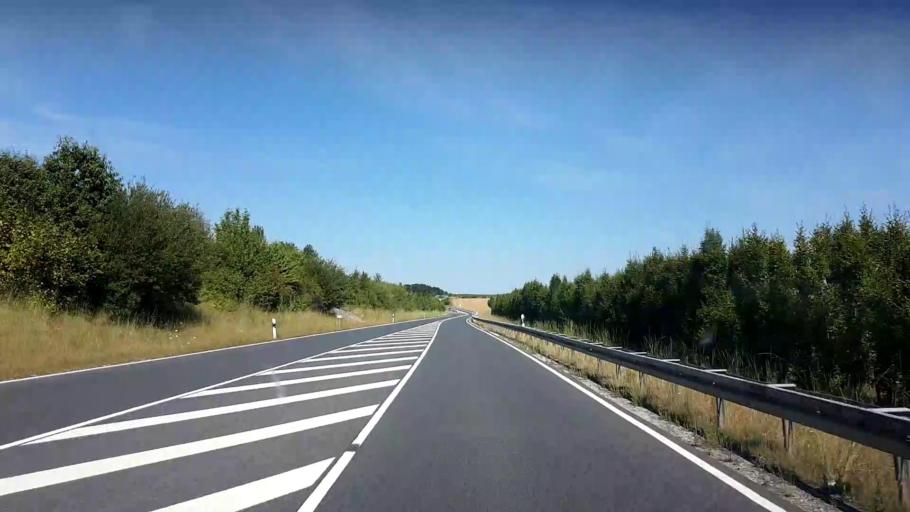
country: DE
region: Bavaria
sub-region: Upper Franconia
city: Untersiemau
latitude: 50.1723
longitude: 10.9895
